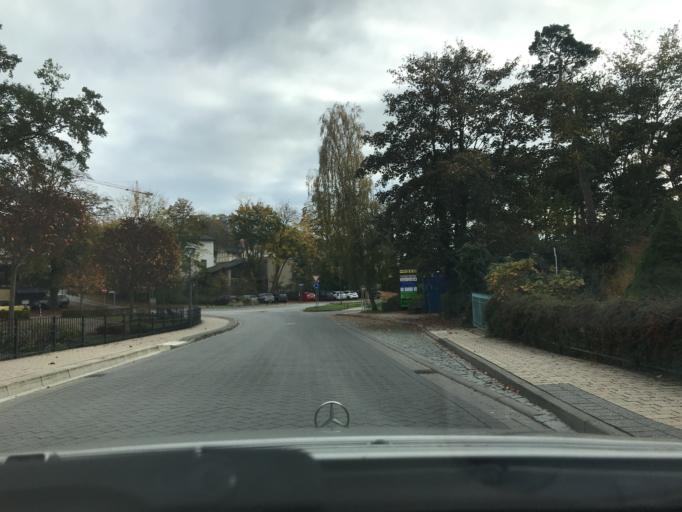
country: DE
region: Mecklenburg-Vorpommern
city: Seebad Heringsdorf
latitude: 53.9618
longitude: 14.1583
